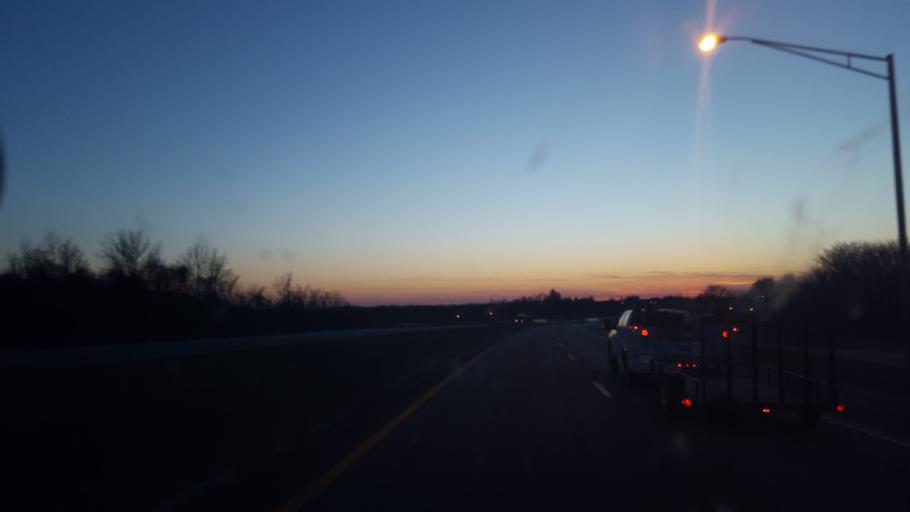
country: US
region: Ohio
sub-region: Belmont County
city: Barnesville
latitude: 40.0555
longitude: -81.2253
